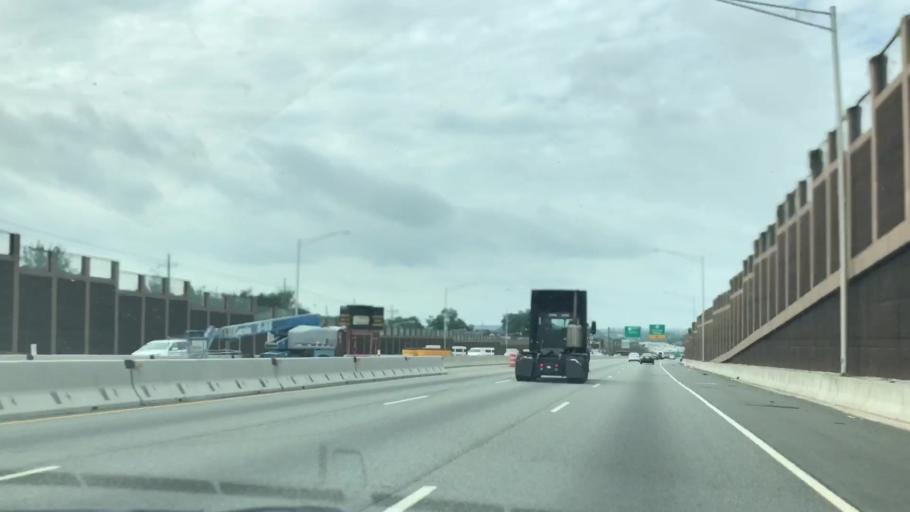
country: US
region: New Jersey
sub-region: Bergen County
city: Lyndhurst
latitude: 40.8171
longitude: -74.1139
